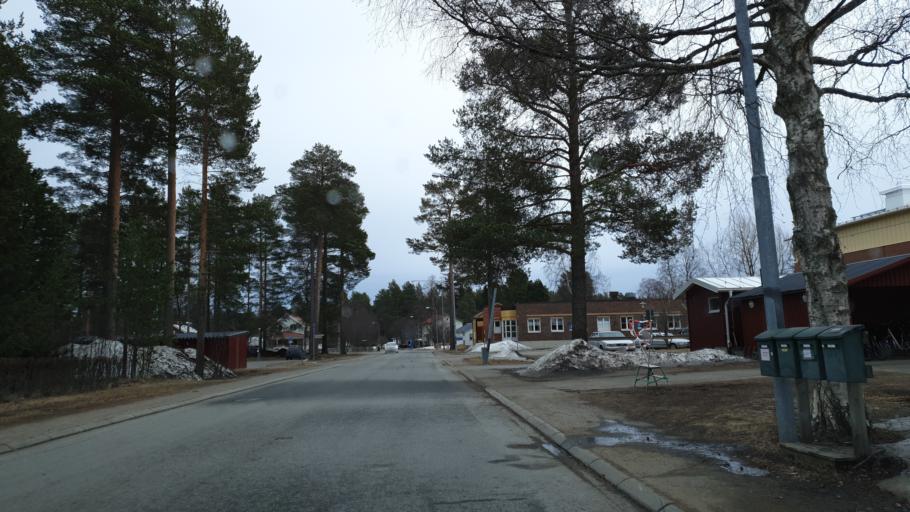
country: SE
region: Vaesterbotten
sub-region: Skelleftea Kommun
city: Byske
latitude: 64.9512
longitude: 21.2061
